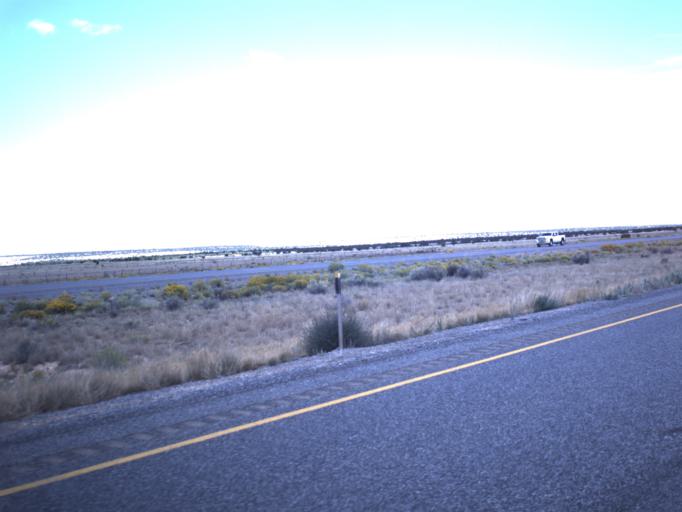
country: US
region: Utah
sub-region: Emery County
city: Castle Dale
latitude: 38.8925
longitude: -110.6289
